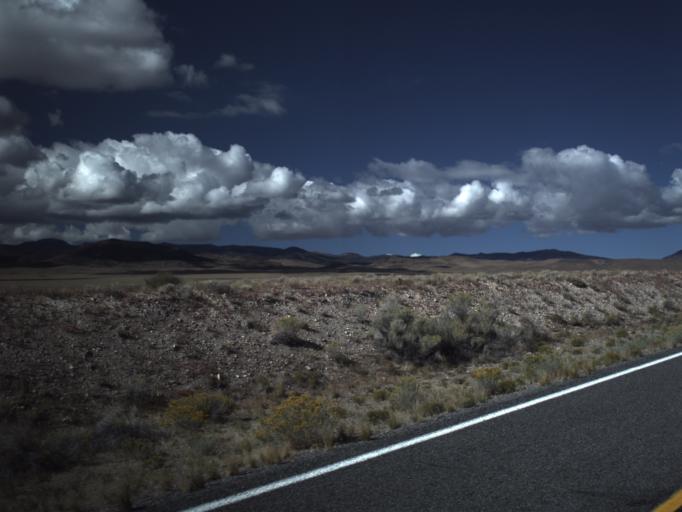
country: US
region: Utah
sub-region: Beaver County
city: Milford
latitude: 38.5690
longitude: -113.7813
